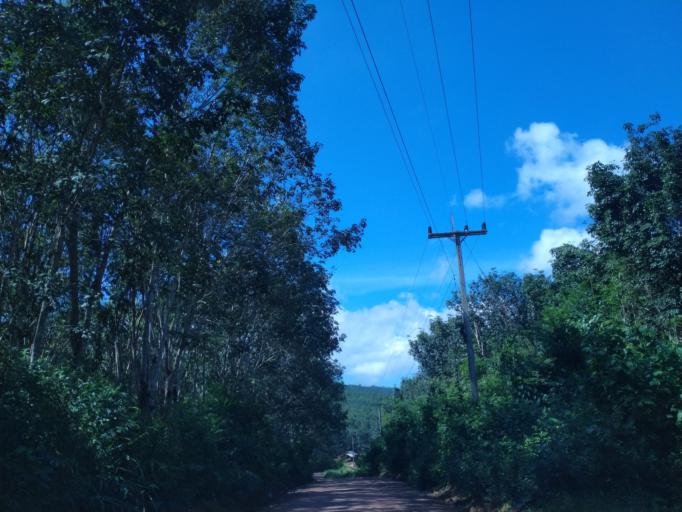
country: TH
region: Changwat Bueng Kan
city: Pak Khat
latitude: 18.6392
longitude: 102.9844
